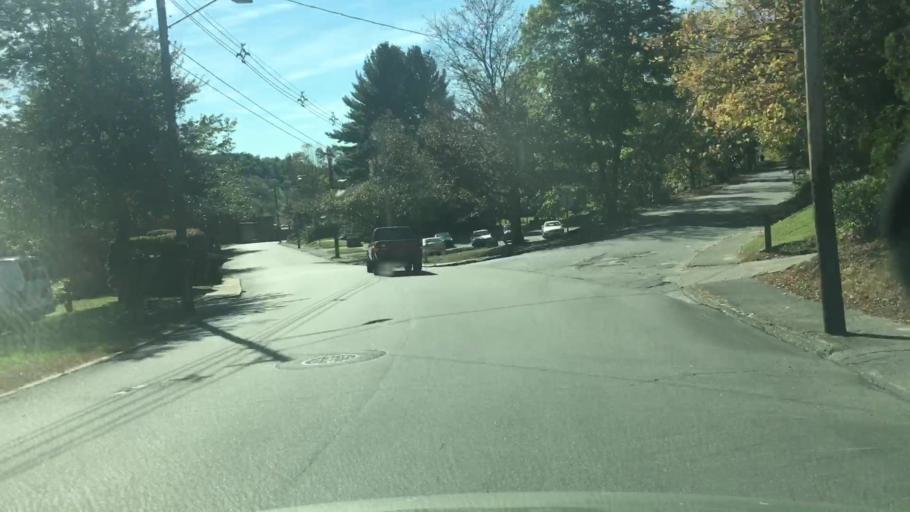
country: US
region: Connecticut
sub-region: Tolland County
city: Stafford Springs
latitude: 41.9572
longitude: -72.3022
